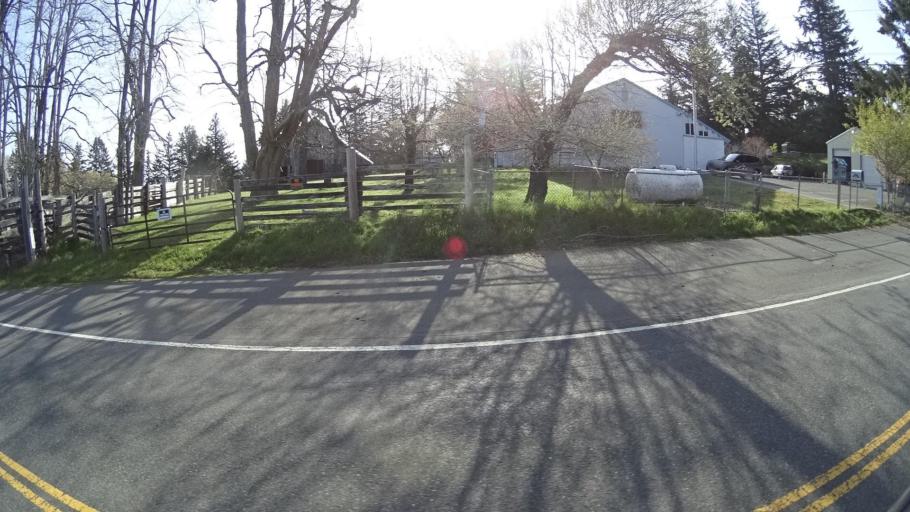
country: US
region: California
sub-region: Humboldt County
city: Blue Lake
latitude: 40.7266
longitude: -123.9449
